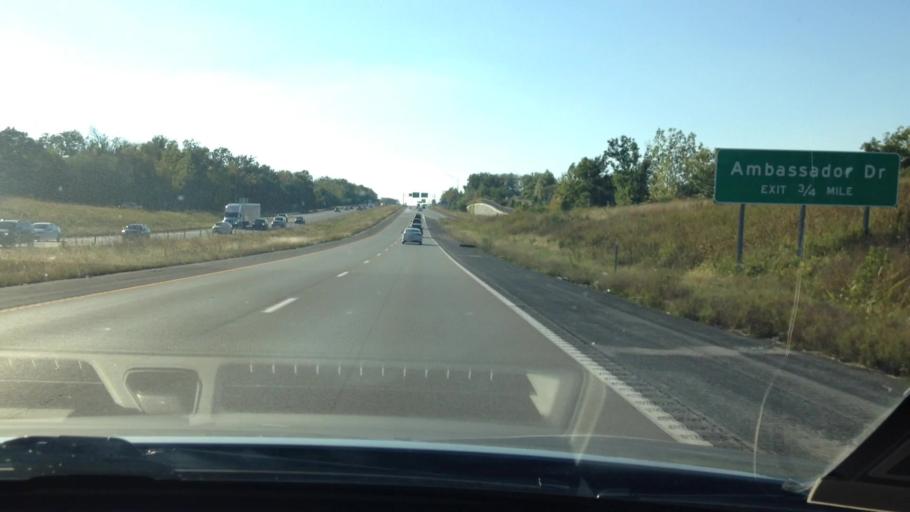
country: US
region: Missouri
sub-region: Platte County
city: Weatherby Lake
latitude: 39.2544
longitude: -94.6328
